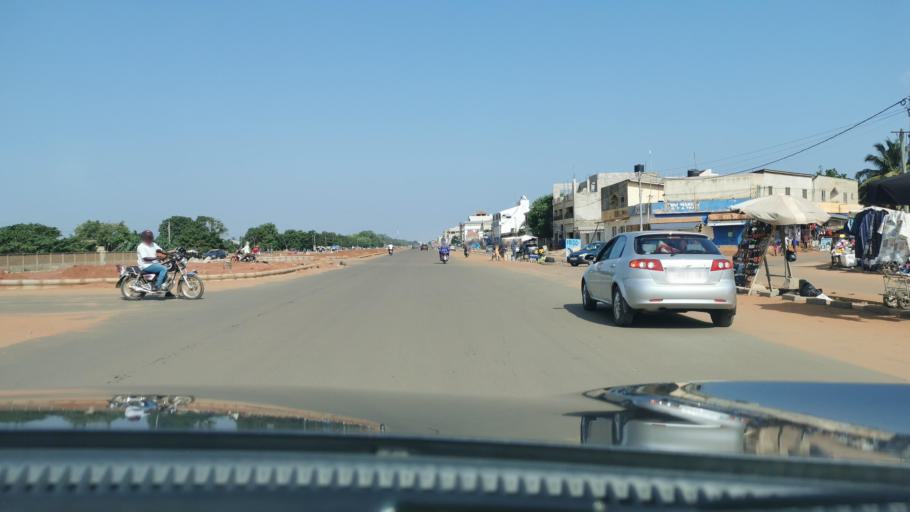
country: TG
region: Maritime
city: Lome
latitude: 6.1995
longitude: 1.1499
